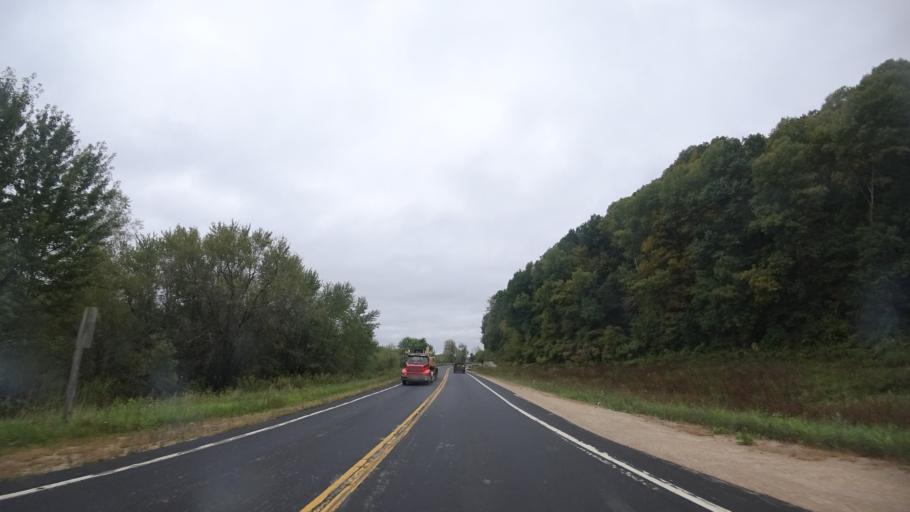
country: US
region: Wisconsin
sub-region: Grant County
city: Boscobel
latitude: 43.1509
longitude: -90.7211
